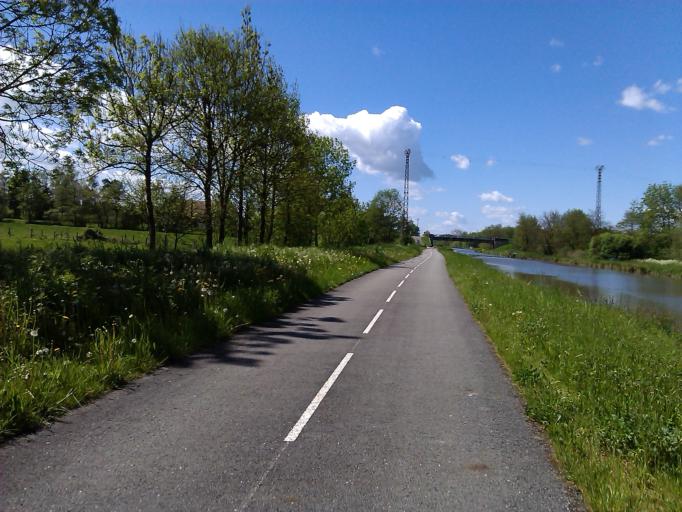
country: FR
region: Franche-Comte
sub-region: Territoire de Belfort
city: Montreux-Chateau
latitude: 47.5838
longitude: 6.9688
